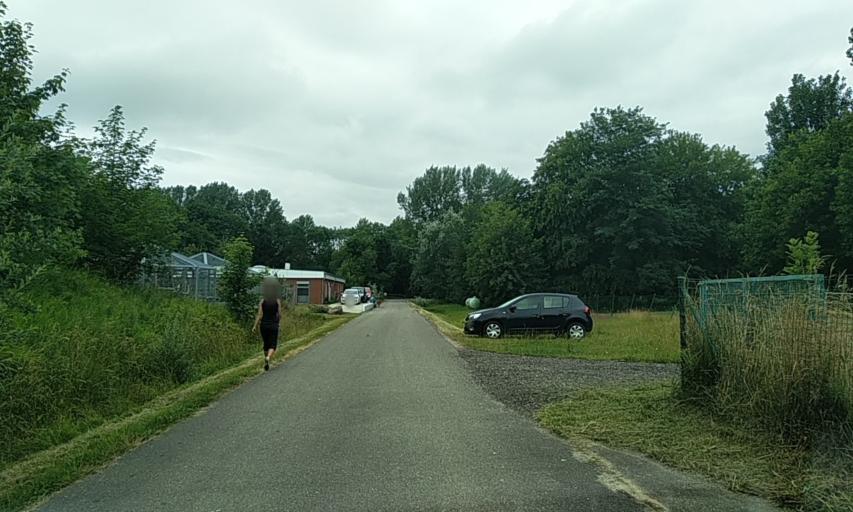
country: DE
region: Schleswig-Holstein
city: Brodersby
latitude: 54.6455
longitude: 10.0095
